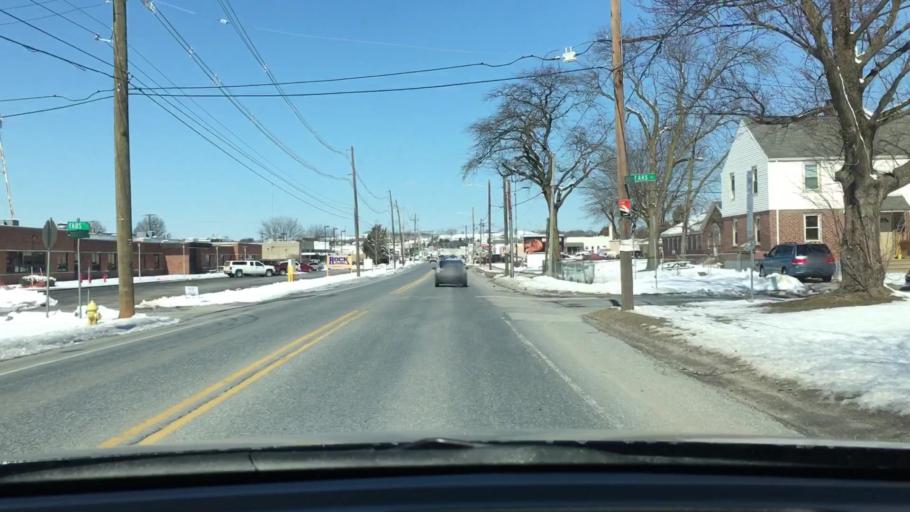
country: US
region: Pennsylvania
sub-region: York County
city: North York
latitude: 39.9742
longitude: -76.7542
